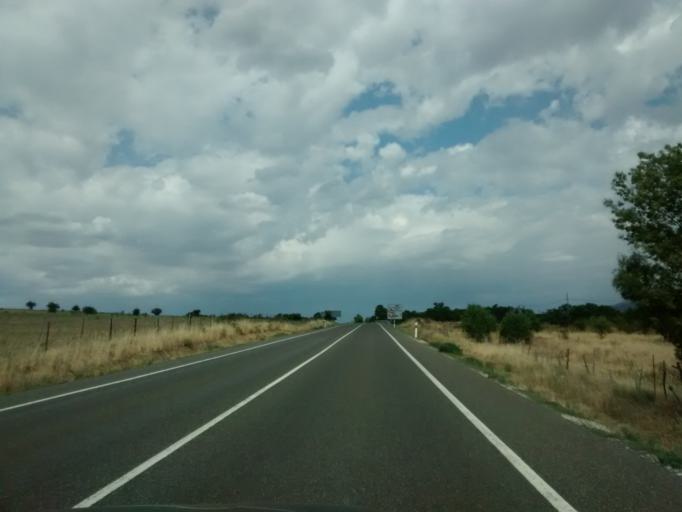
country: ES
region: Castille and Leon
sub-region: Provincia de Segovia
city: Navafria
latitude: 41.0665
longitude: -3.8194
